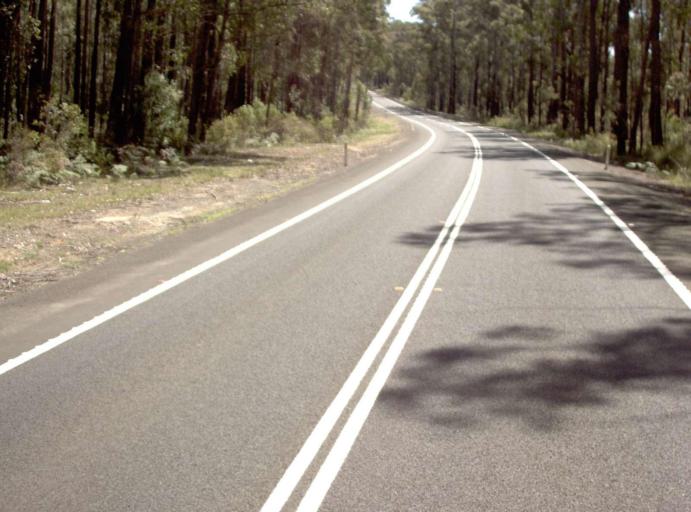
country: AU
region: New South Wales
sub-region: Bombala
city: Bombala
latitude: -37.5652
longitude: 149.0449
